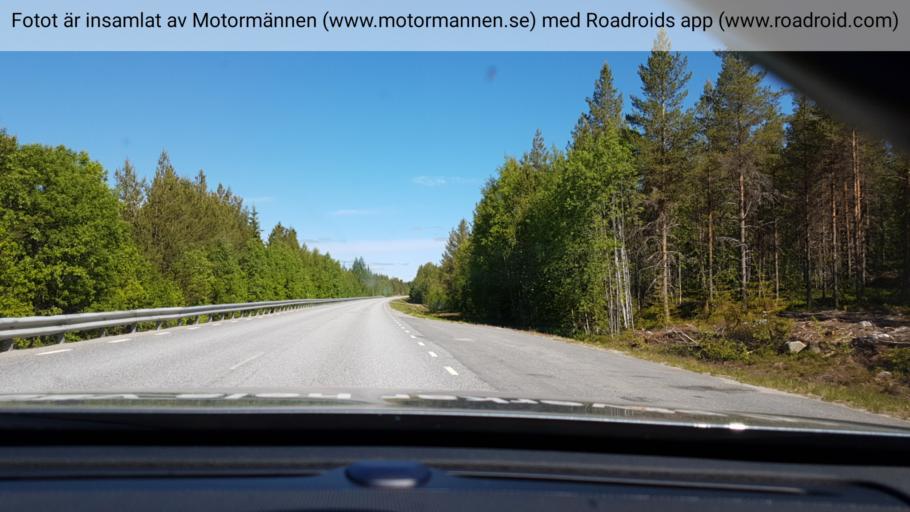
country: SE
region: Vaesterbotten
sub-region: Vilhelmina Kommun
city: Vilhelmina
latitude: 64.4284
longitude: 16.8028
